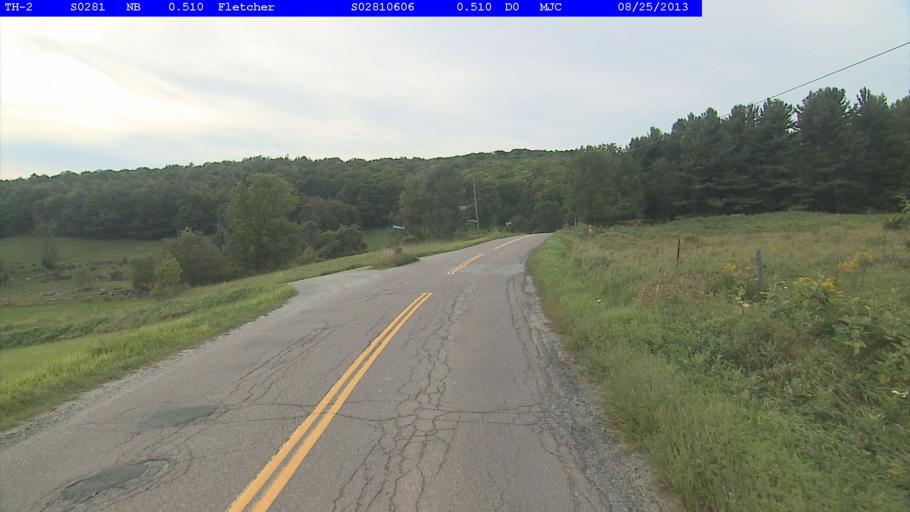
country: US
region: Vermont
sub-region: Chittenden County
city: Milton
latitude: 44.6868
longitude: -72.9234
